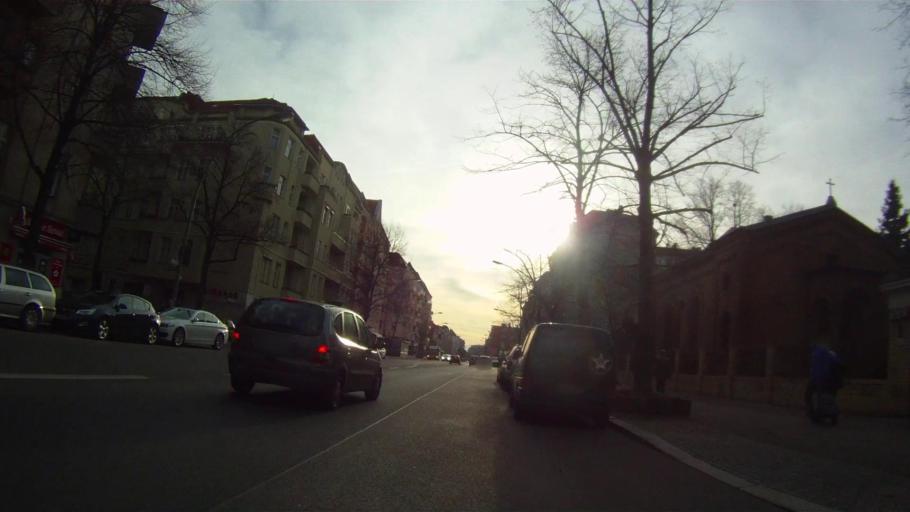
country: DE
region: Berlin
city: Britz
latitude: 52.4694
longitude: 13.4302
